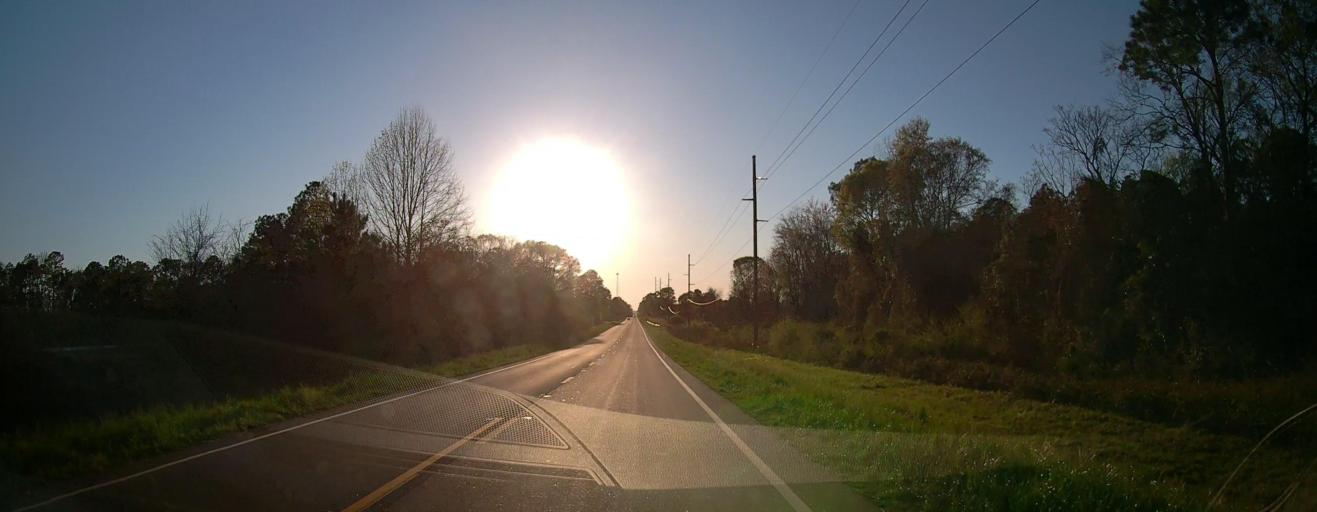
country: US
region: Georgia
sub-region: Wilcox County
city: Rochelle
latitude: 31.9506
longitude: -83.4683
